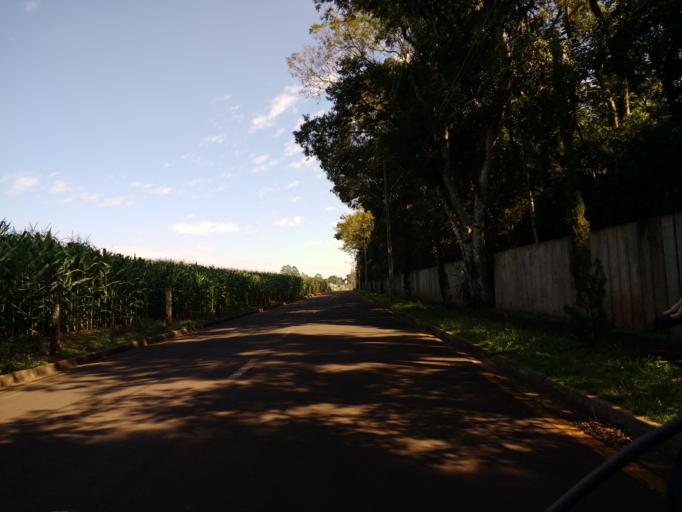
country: BR
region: Parana
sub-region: Londrina
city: Londrina
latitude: -23.3669
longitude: -51.1887
